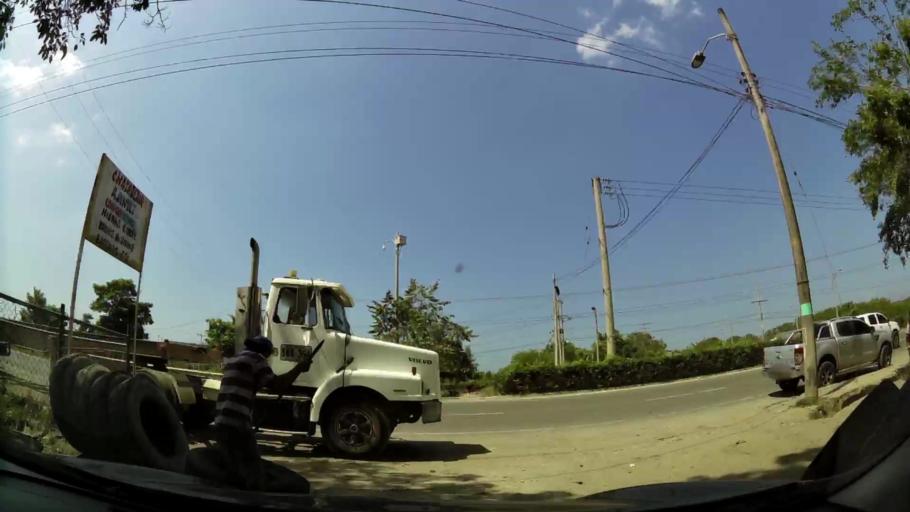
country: CO
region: Bolivar
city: Cartagena
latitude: 10.3451
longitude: -75.4947
